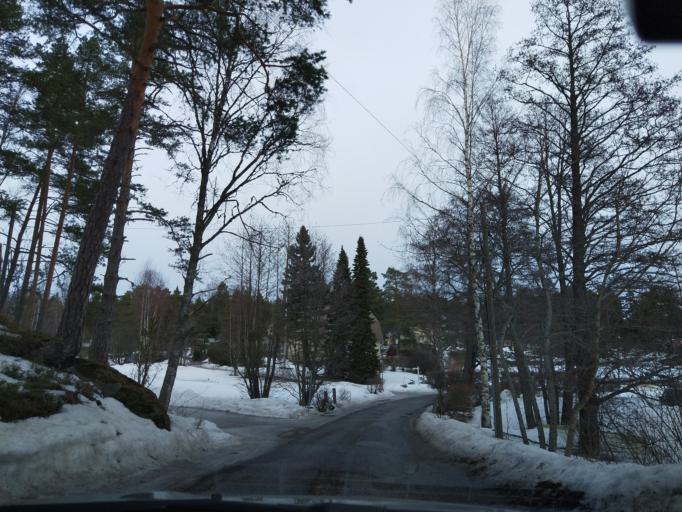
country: FI
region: Uusimaa
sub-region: Helsinki
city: Sibbo
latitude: 60.2562
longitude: 25.3018
